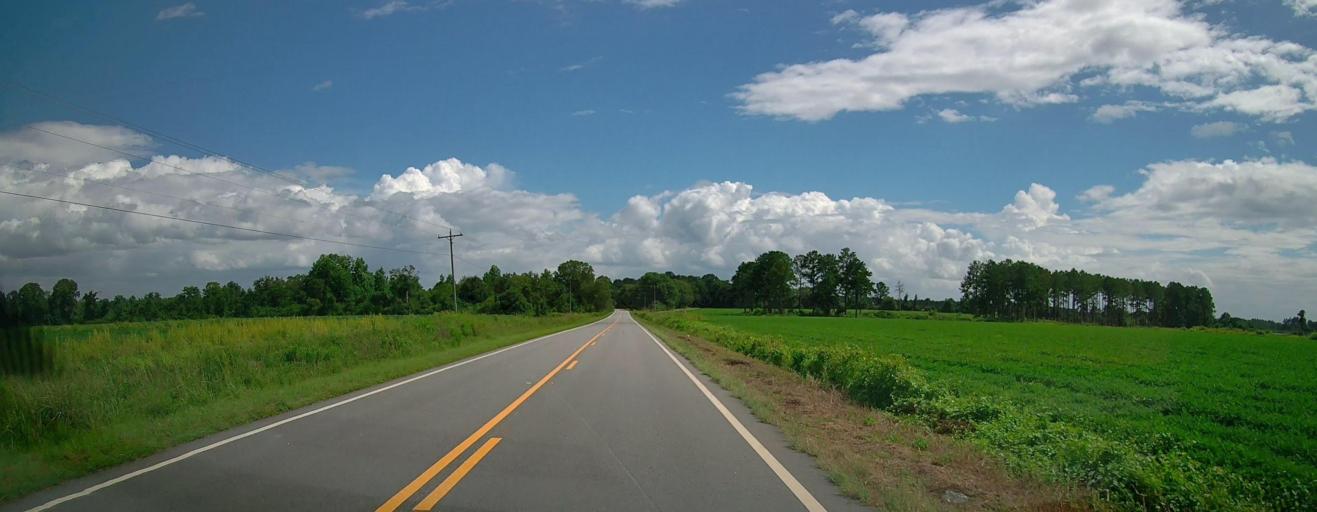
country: US
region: Georgia
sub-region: Irwin County
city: Ocilla
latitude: 31.6457
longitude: -83.1727
